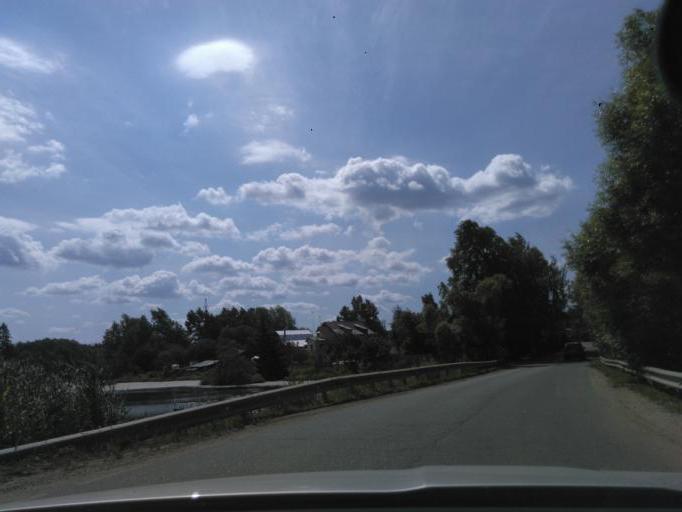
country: RU
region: Moskovskaya
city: Solnechnogorsk
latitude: 56.1646
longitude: 36.9766
